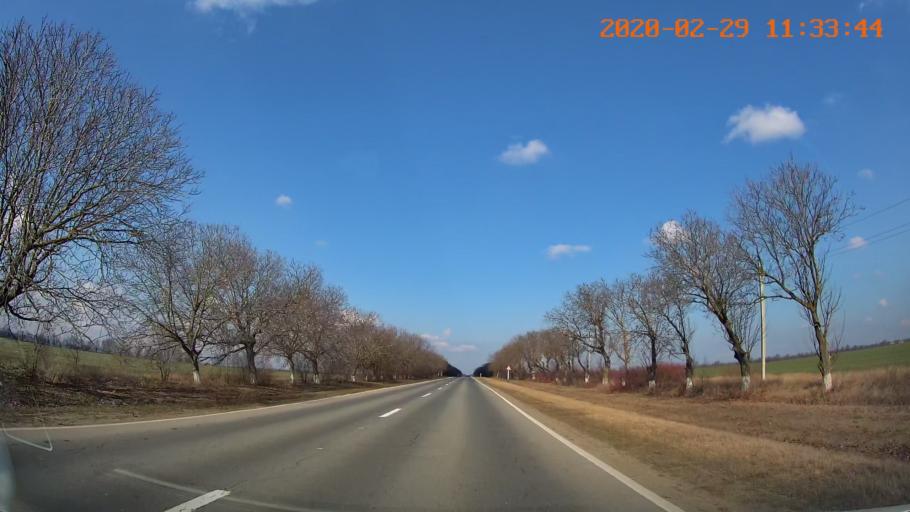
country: MD
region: Rezina
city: Saharna
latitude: 47.5556
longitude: 29.0814
